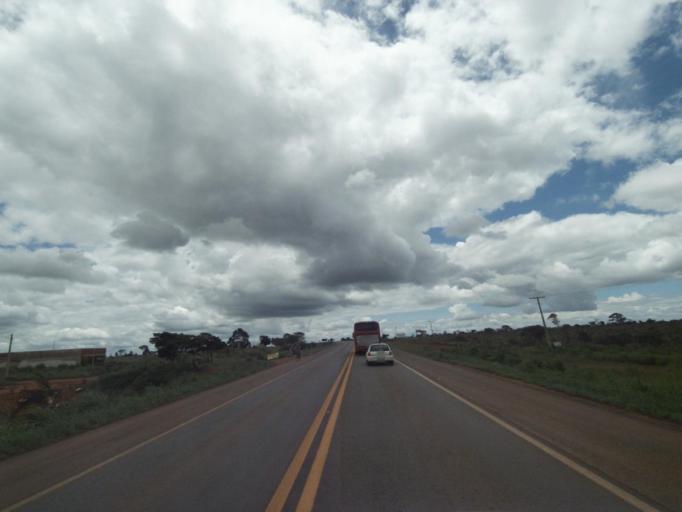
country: BR
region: Federal District
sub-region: Brasilia
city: Brasilia
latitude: -15.7396
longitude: -48.3865
